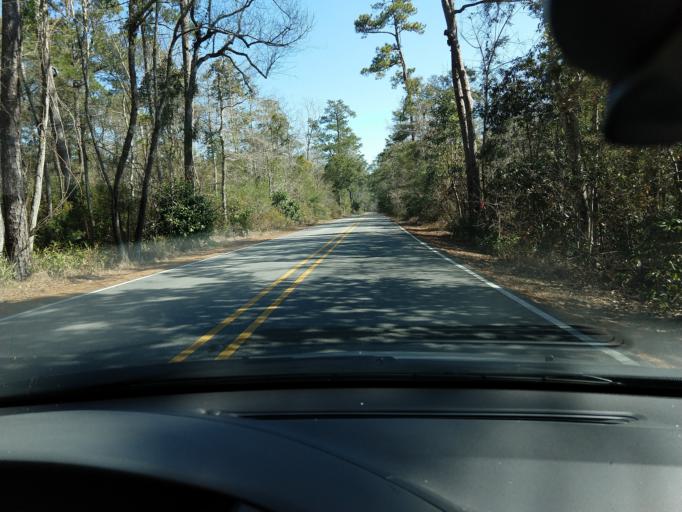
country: US
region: Mississippi
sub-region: Jackson County
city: Gulf Park Estates
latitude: 30.3962
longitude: -88.7849
